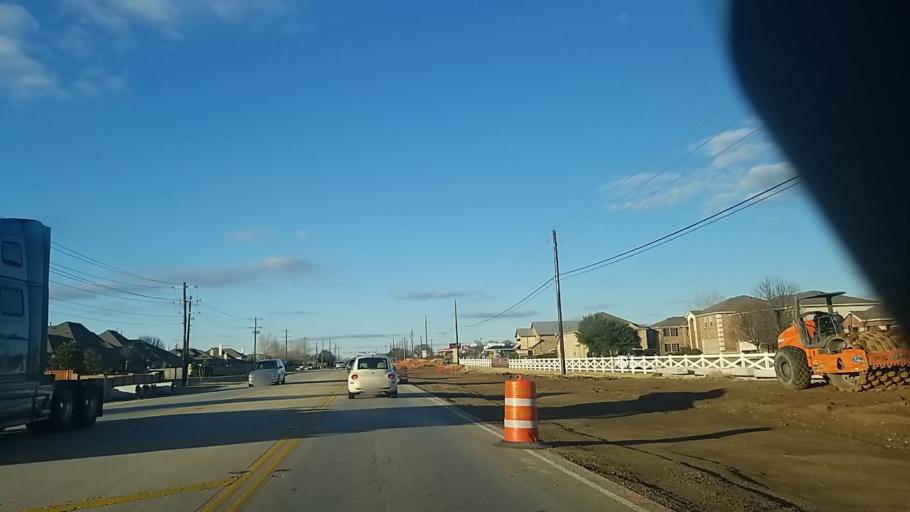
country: US
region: Texas
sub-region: Denton County
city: Corinth
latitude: 33.1549
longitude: -97.1055
